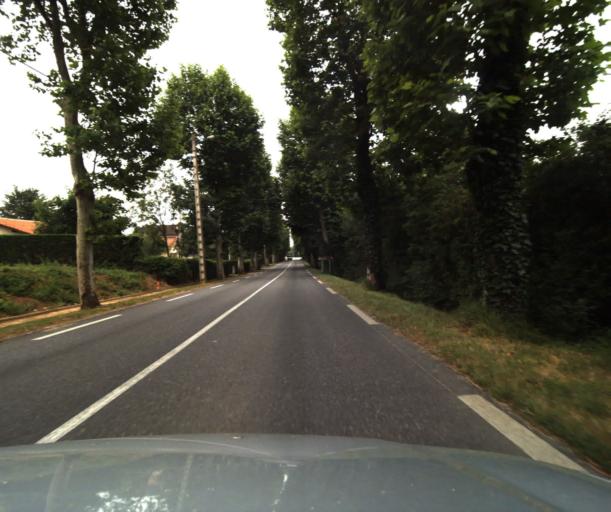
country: FR
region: Midi-Pyrenees
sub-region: Departement du Gers
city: Gimont
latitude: 43.7262
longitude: 0.8757
